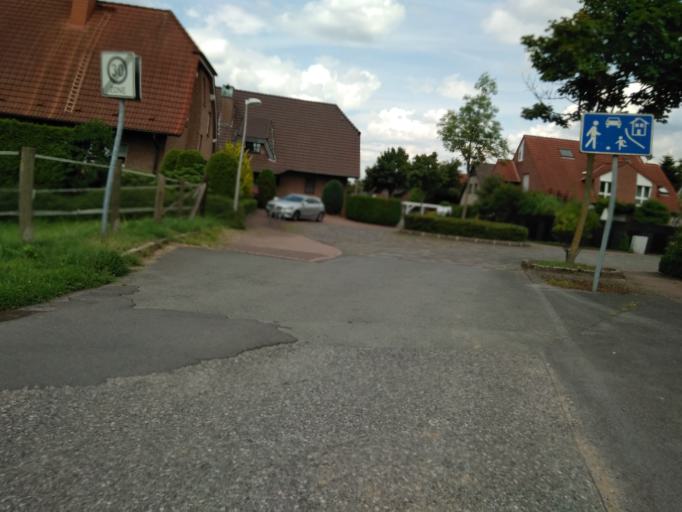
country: DE
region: North Rhine-Westphalia
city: Dorsten
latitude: 51.6620
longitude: 6.9482
